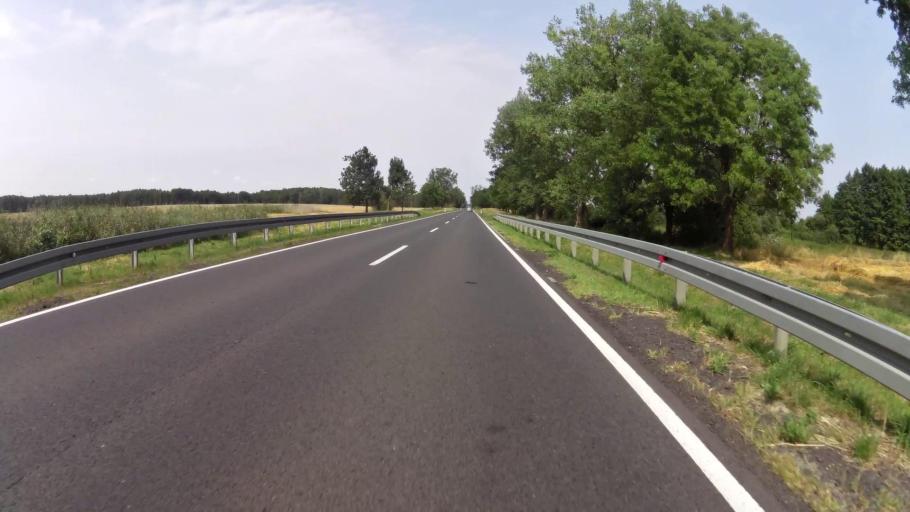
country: PL
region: West Pomeranian Voivodeship
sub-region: Powiat gryfinski
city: Mieszkowice
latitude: 52.8287
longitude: 14.4949
